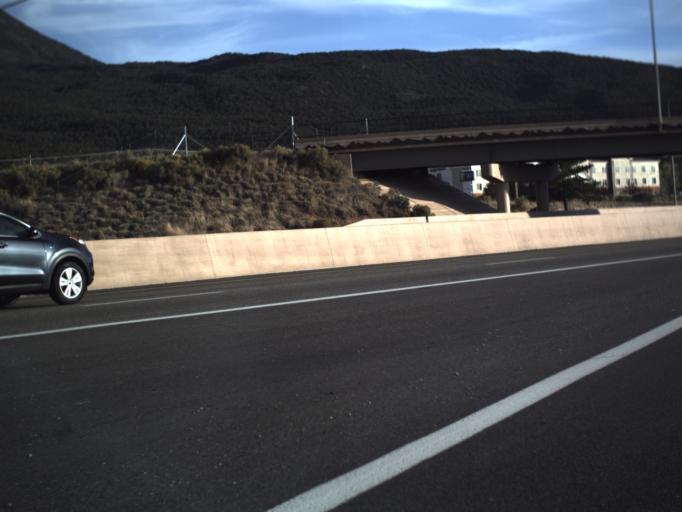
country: US
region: Utah
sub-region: Iron County
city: Cedar City
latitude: 37.6523
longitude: -113.0837
